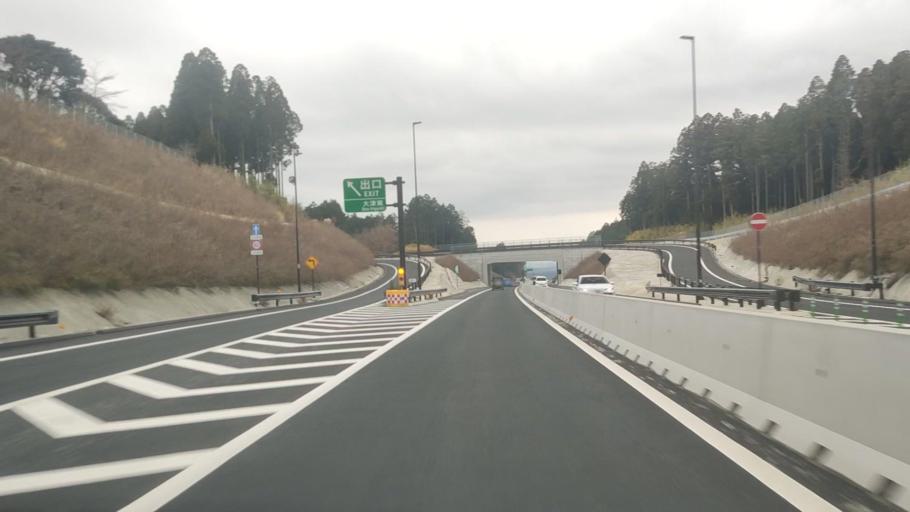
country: JP
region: Kumamoto
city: Ozu
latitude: 32.8998
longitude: 130.9310
